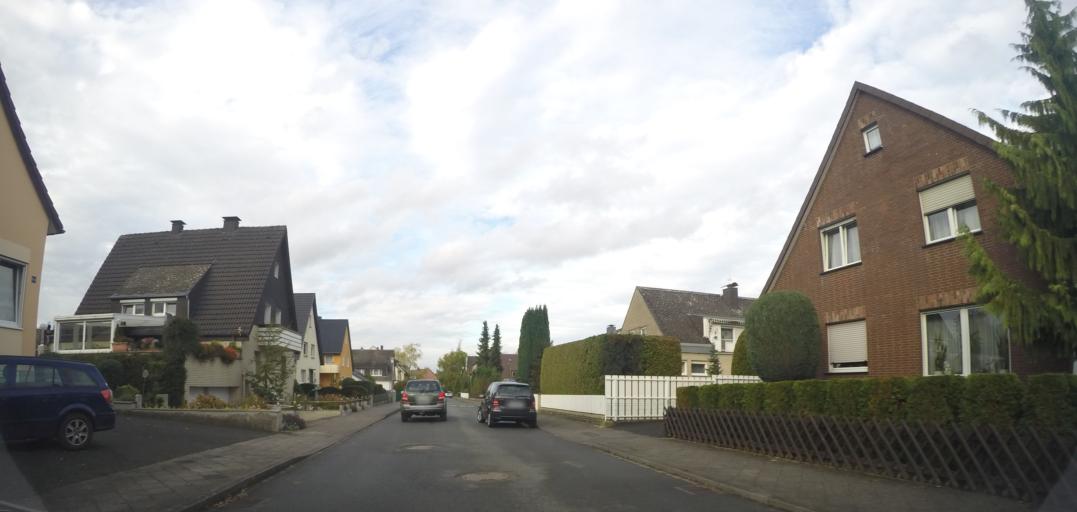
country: DE
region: North Rhine-Westphalia
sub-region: Regierungsbezirk Arnsberg
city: Lippstadt
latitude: 51.6617
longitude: 8.3358
